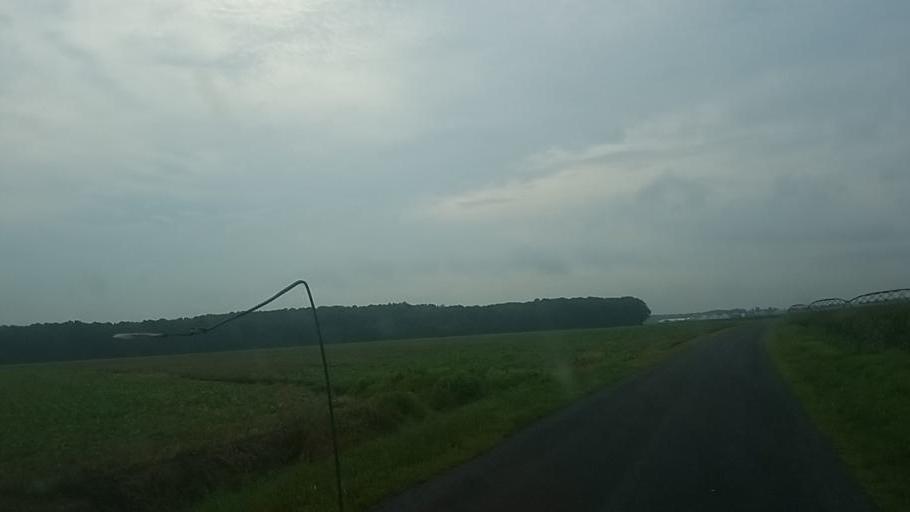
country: US
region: Delaware
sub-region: Sussex County
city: Selbyville
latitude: 38.4478
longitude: -75.2771
